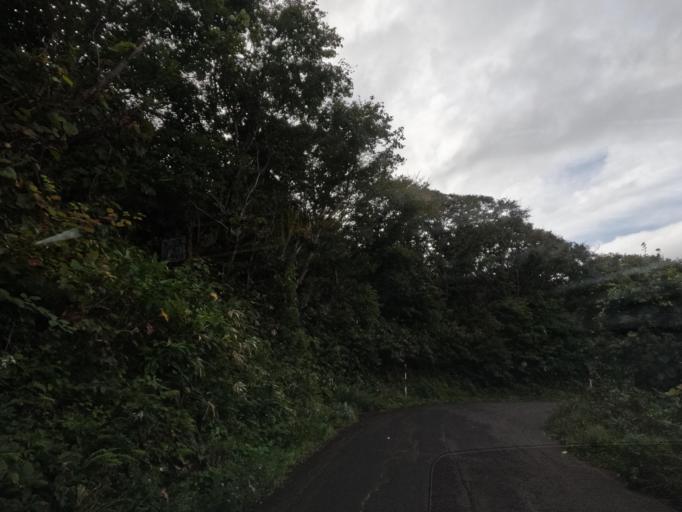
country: JP
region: Hokkaido
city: Muroran
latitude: 42.3304
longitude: 141.0035
